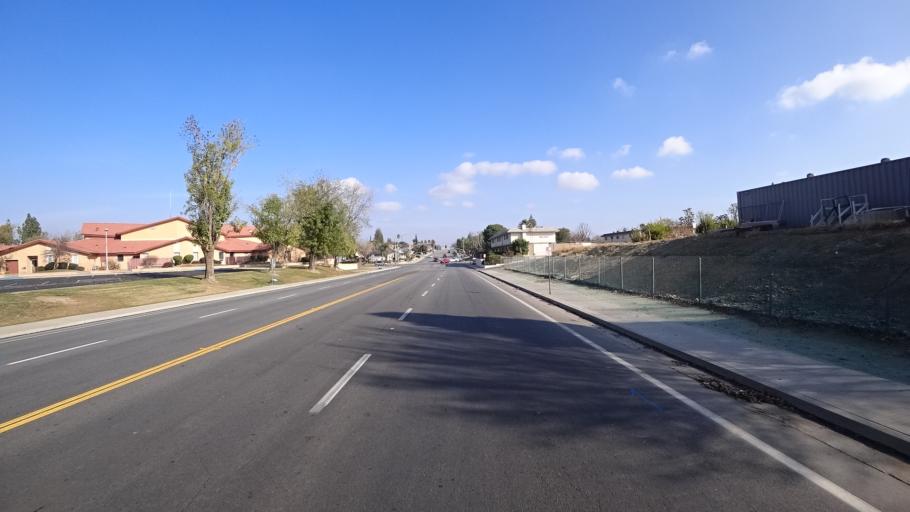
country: US
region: California
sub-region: Kern County
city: Oildale
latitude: 35.4028
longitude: -118.9316
